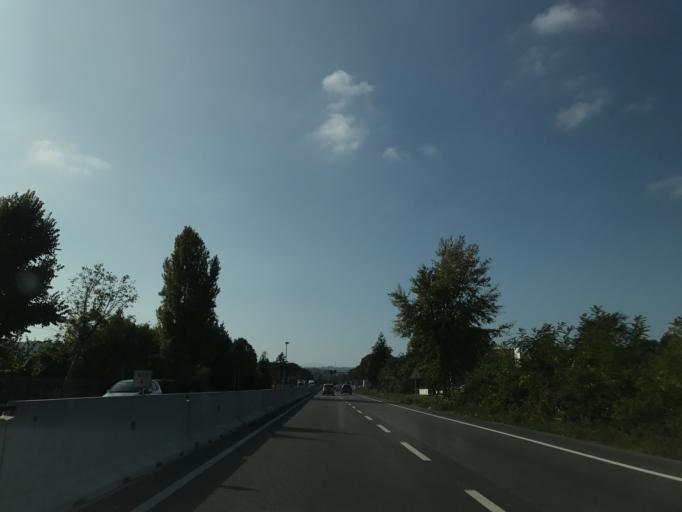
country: IT
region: Emilia-Romagna
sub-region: Provincia di Rimini
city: Cerasolo
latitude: 43.9975
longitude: 12.5406
